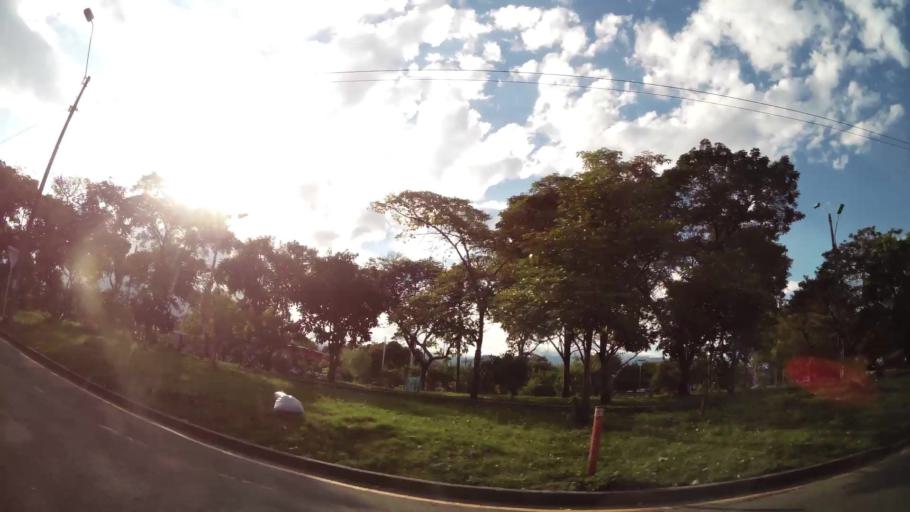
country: CO
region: Valle del Cauca
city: Cali
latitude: 3.4379
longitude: -76.4937
